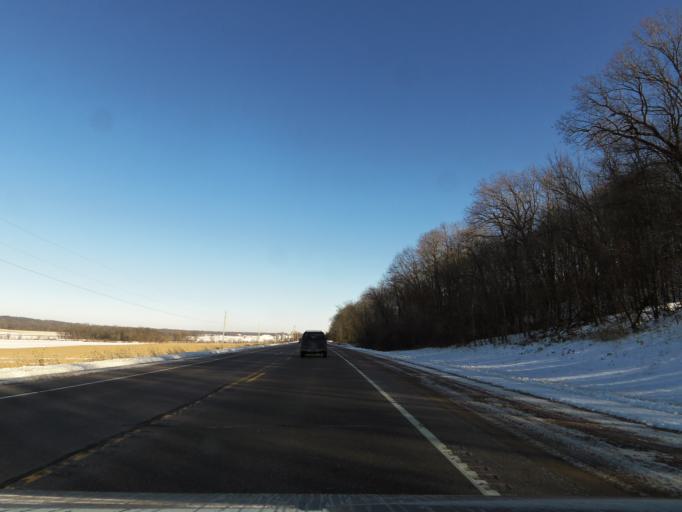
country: US
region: Wisconsin
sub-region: Columbia County
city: Lake Wisconsin
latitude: 43.5045
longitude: -89.6057
